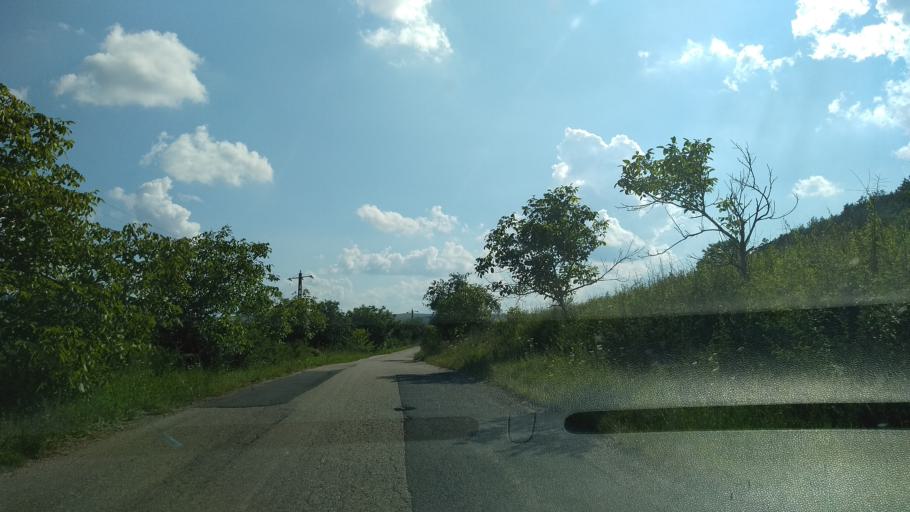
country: RO
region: Hunedoara
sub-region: Comuna Bosorod
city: Bosorod
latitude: 45.7023
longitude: 23.0994
